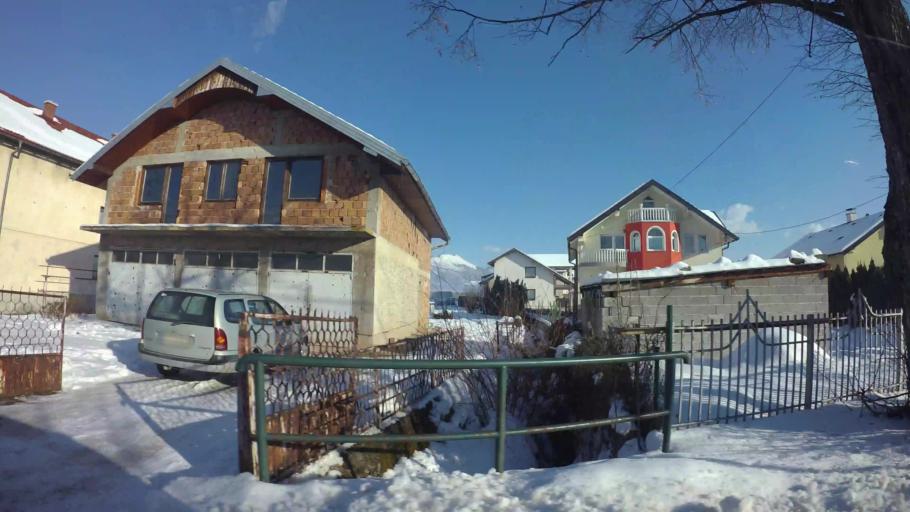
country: BA
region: Federation of Bosnia and Herzegovina
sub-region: Kanton Sarajevo
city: Sarajevo
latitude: 43.8208
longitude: 18.3307
